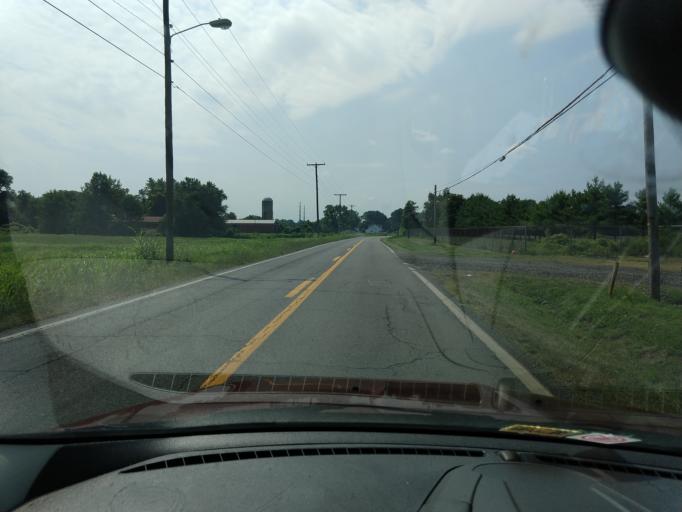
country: US
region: West Virginia
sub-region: Mason County
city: New Haven
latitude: 38.9571
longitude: -81.9235
